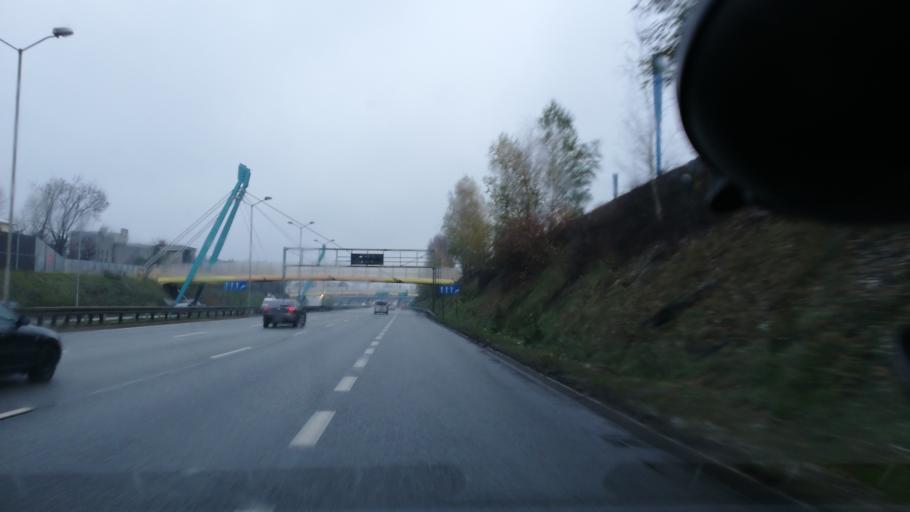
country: PL
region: Silesian Voivodeship
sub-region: Swietochlowice
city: Swietochlowice
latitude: 50.2842
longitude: 18.9434
